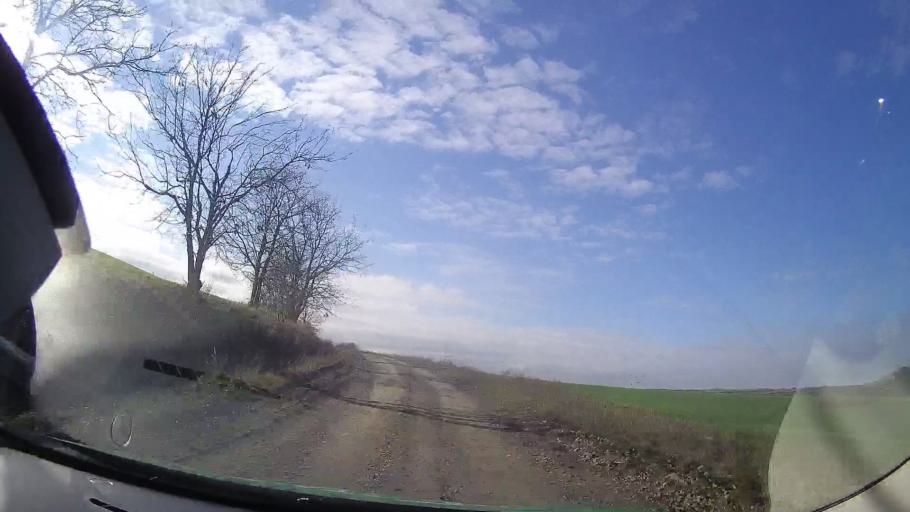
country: RO
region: Mures
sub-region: Comuna Saulia
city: Saulia
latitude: 46.6116
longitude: 24.2490
